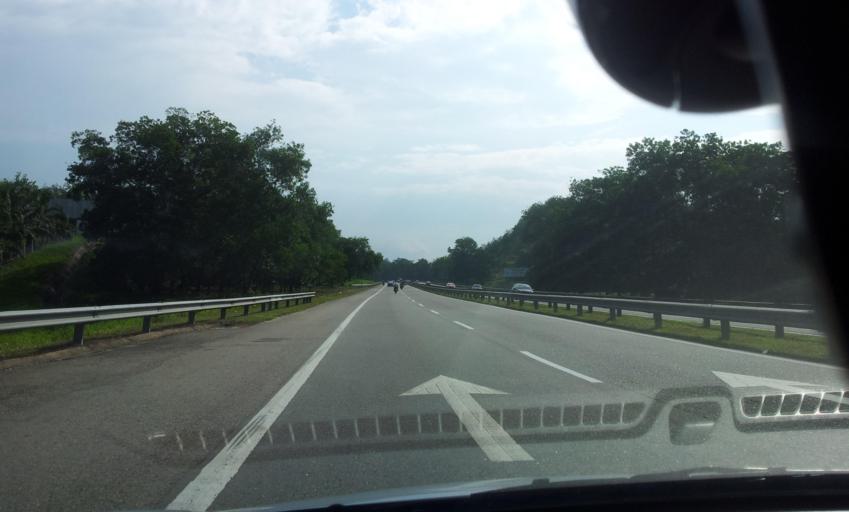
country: MY
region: Pahang
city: Bentong Town
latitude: 3.4925
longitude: 102.0962
